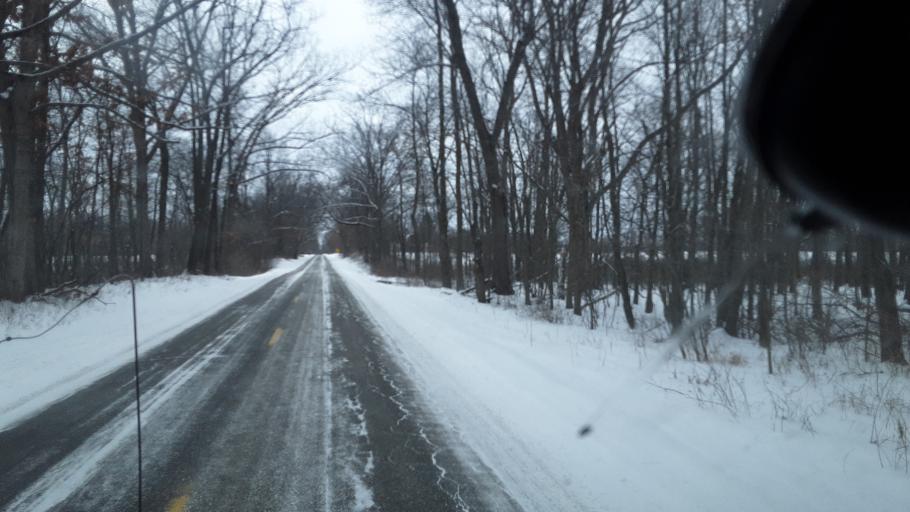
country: US
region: Michigan
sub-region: Ingham County
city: Leslie
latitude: 42.5054
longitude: -84.3892
